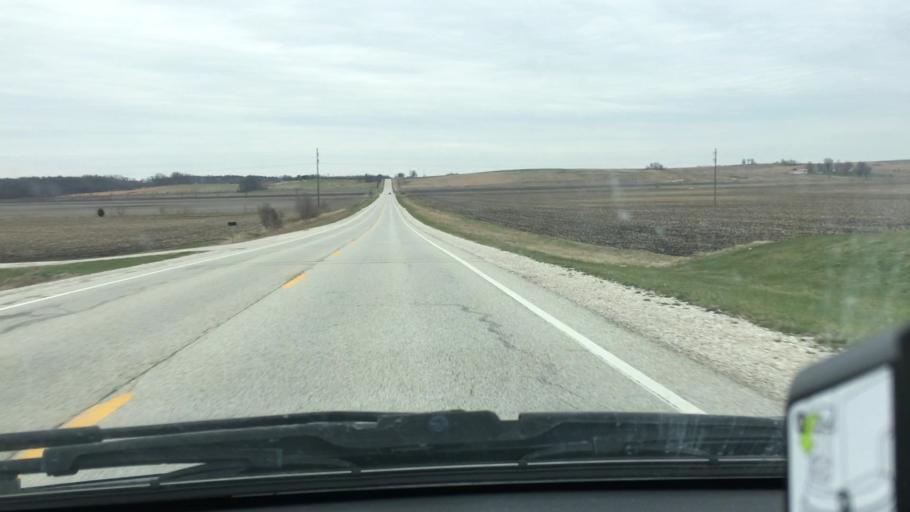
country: US
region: Indiana
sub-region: Greene County
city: Bloomfield
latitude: 38.9996
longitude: -87.0160
